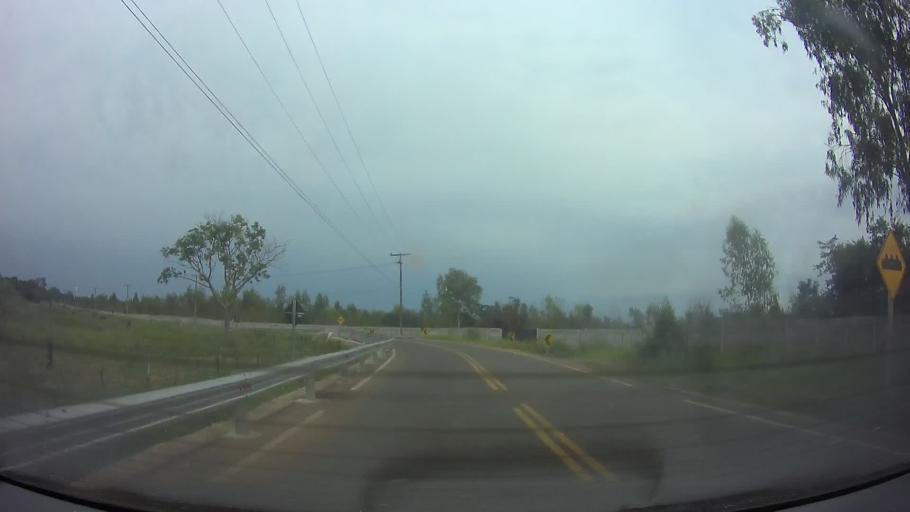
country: PY
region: Central
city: Limpio
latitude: -25.2136
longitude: -57.4830
